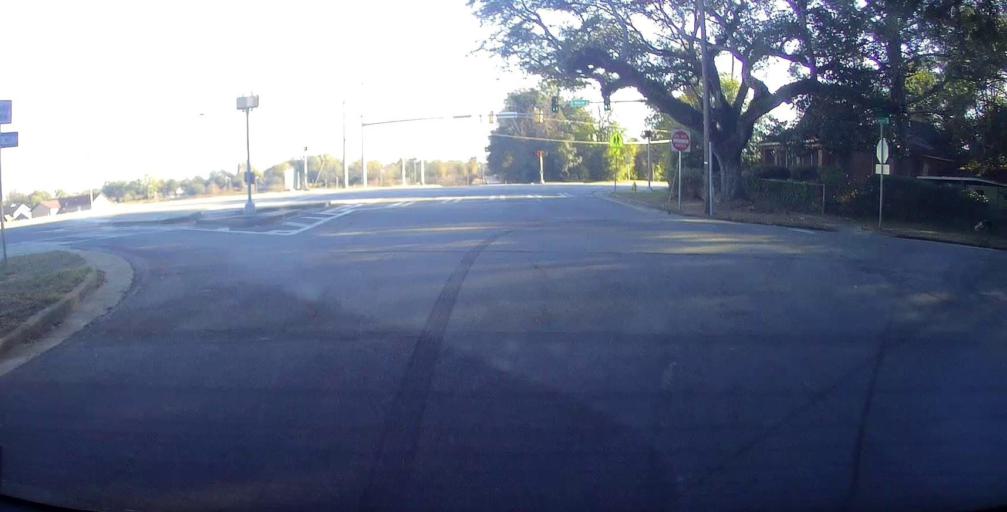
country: US
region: Georgia
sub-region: Dougherty County
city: Albany
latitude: 31.5674
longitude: -84.1591
